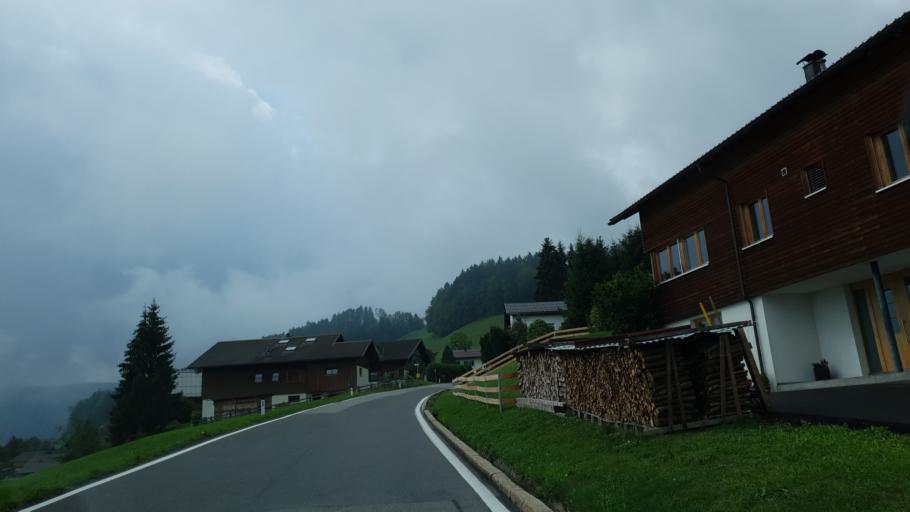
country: AT
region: Vorarlberg
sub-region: Politischer Bezirk Bregenz
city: Andelsbuch
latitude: 47.4171
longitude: 9.8395
